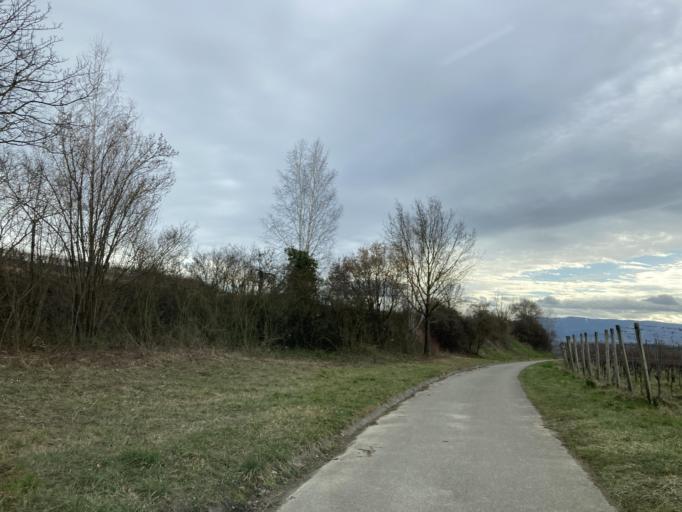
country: DE
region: Baden-Wuerttemberg
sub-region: Freiburg Region
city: Bahlingen
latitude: 48.1093
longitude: 7.7256
